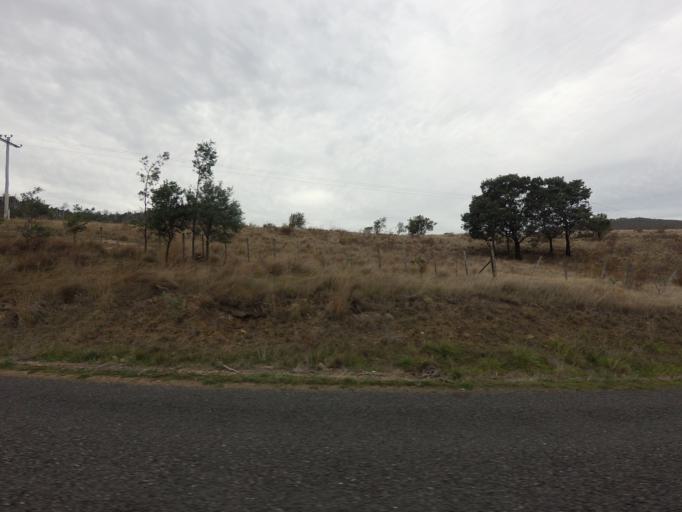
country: AU
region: Tasmania
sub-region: Derwent Valley
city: New Norfolk
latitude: -42.5046
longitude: 146.9462
